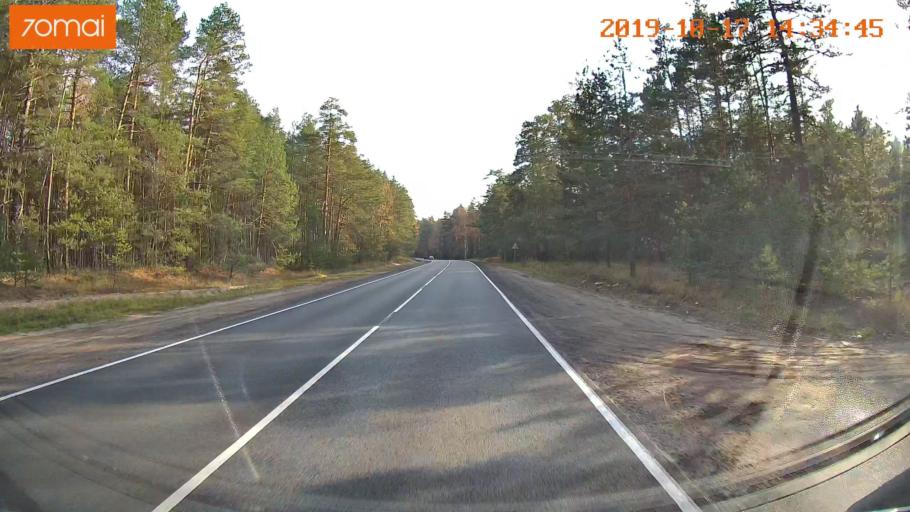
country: RU
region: Rjazan
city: Solotcha
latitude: 54.9081
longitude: 39.9990
